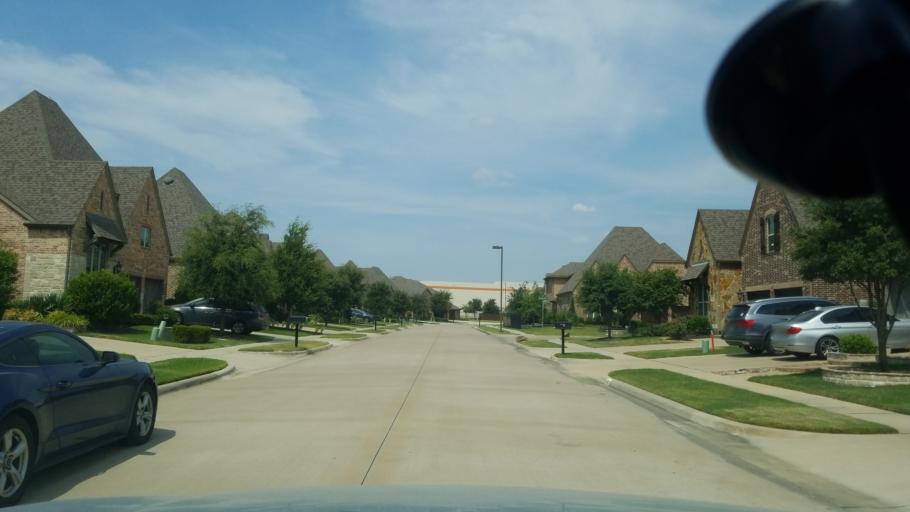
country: US
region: Texas
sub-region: Dallas County
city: Farmers Branch
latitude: 32.8907
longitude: -96.9376
